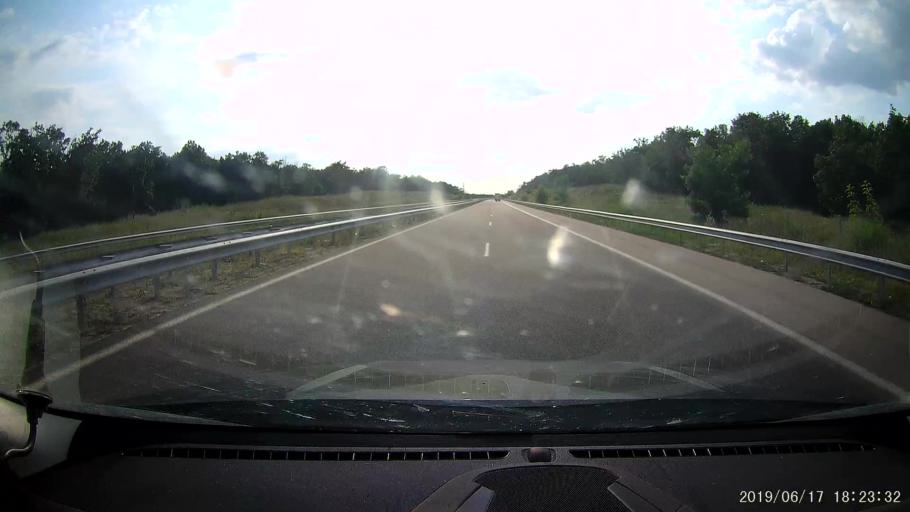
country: BG
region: Khaskovo
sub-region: Obshtina Simeonovgrad
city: Simeonovgrad
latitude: 41.9762
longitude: 25.7183
